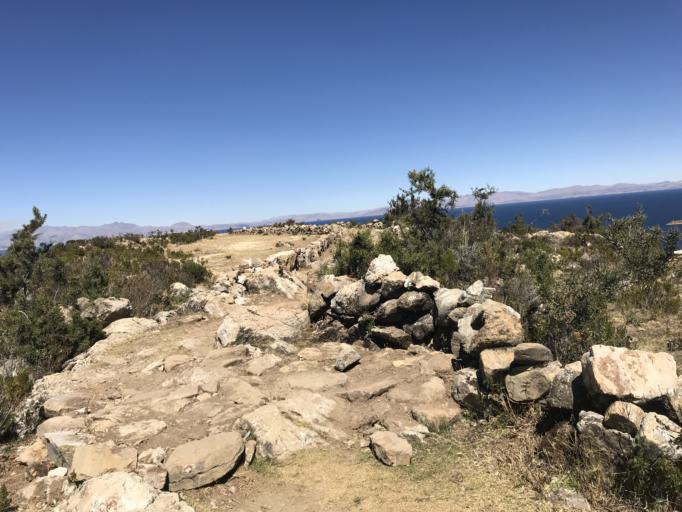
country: BO
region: La Paz
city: Yumani
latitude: -16.0453
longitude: -69.1462
